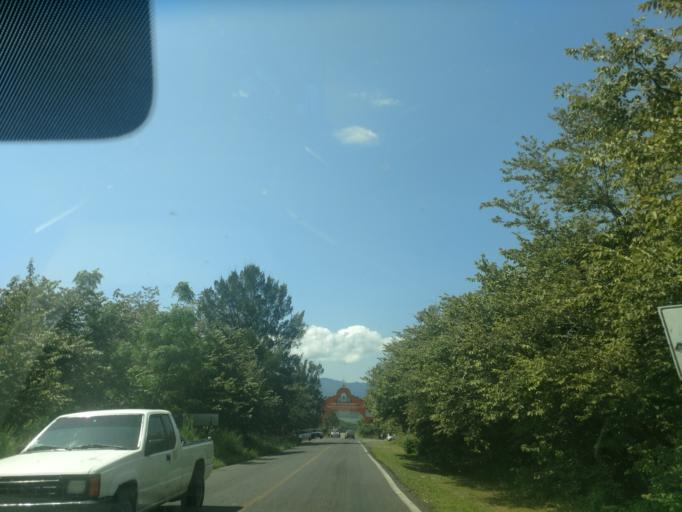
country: MX
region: Jalisco
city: Talpa de Allende
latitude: 20.4003
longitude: -104.8148
